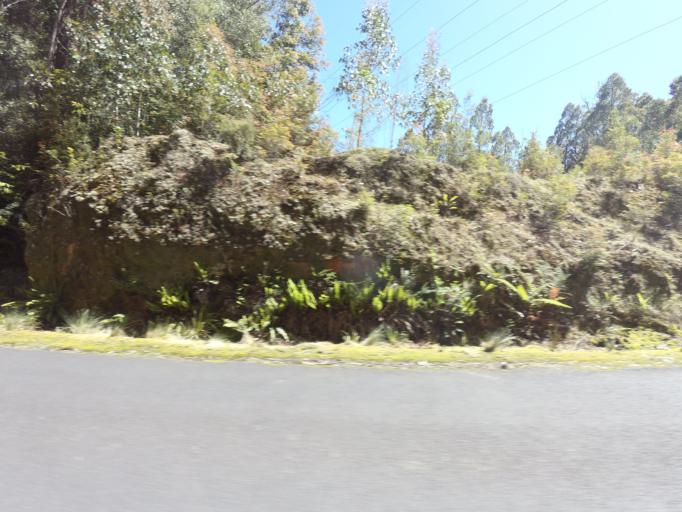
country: AU
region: Tasmania
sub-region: Huon Valley
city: Geeveston
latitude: -42.8183
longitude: 146.3443
